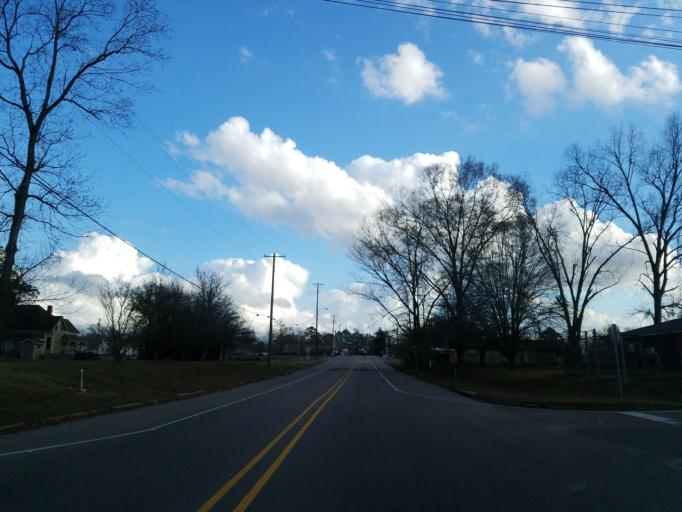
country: US
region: Mississippi
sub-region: Jones County
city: Sharon
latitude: 31.7878
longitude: -89.0357
